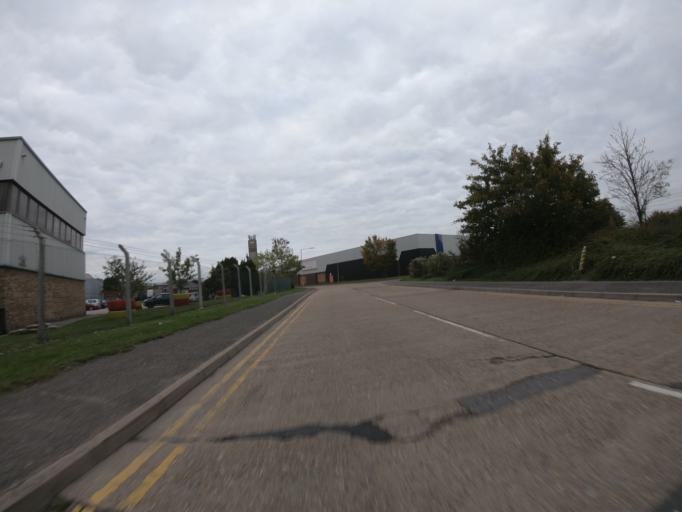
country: GB
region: England
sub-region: Kent
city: West Thurrock
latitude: 51.4833
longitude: 0.2707
